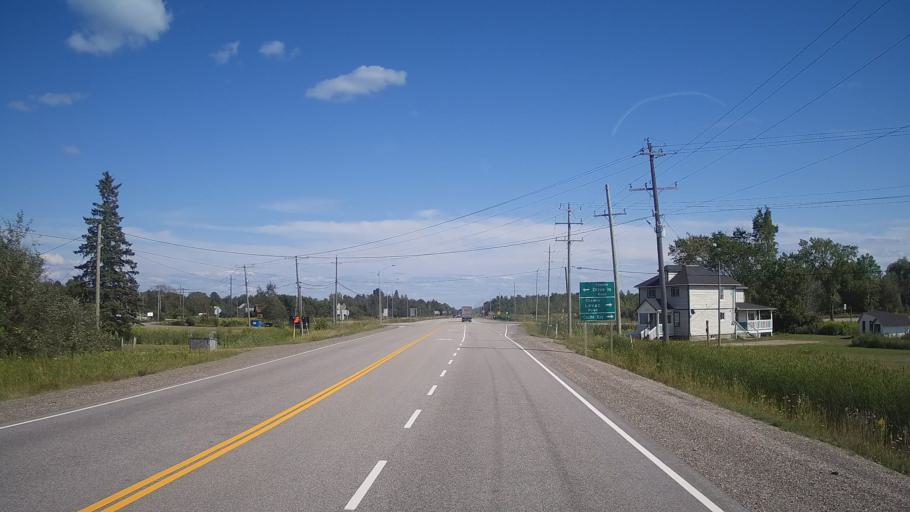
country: CA
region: Ontario
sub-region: Nipissing District
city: North Bay
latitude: 46.3789
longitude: -79.9752
